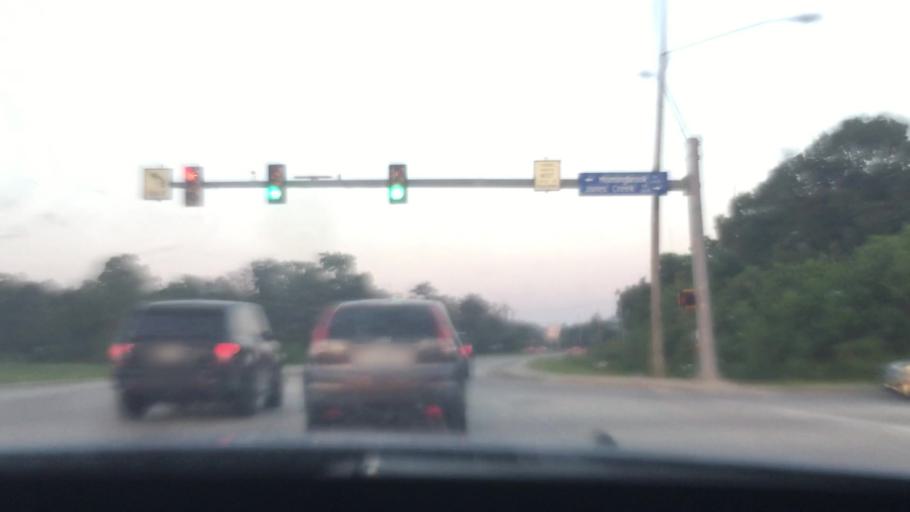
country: US
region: Louisiana
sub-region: East Baton Rouge Parish
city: Shenandoah
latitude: 30.4269
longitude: -91.0143
